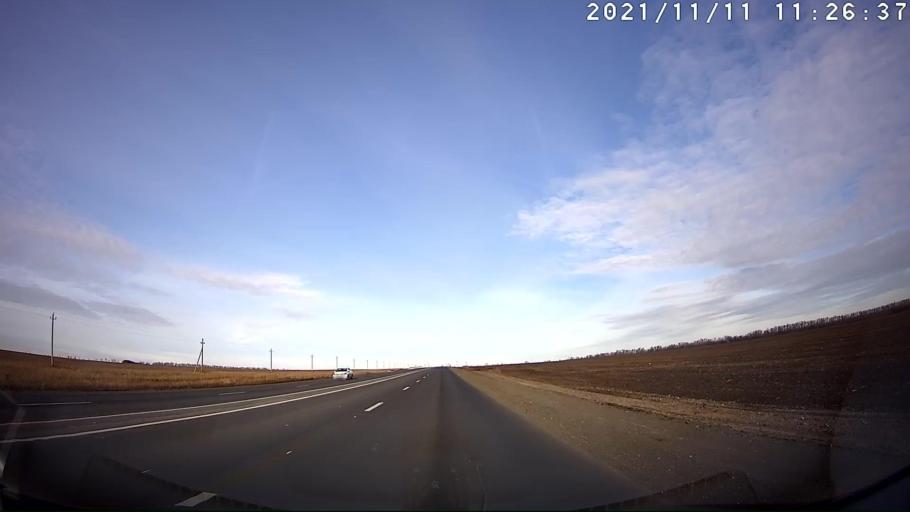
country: RU
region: Samara
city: Syzran'
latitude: 53.2379
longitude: 48.4905
